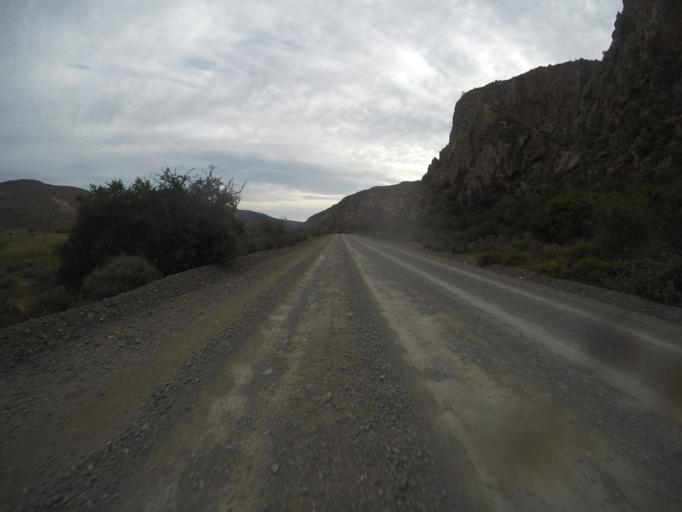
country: ZA
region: Eastern Cape
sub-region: Cacadu District Municipality
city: Willowmore
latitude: -33.5204
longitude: 23.6657
